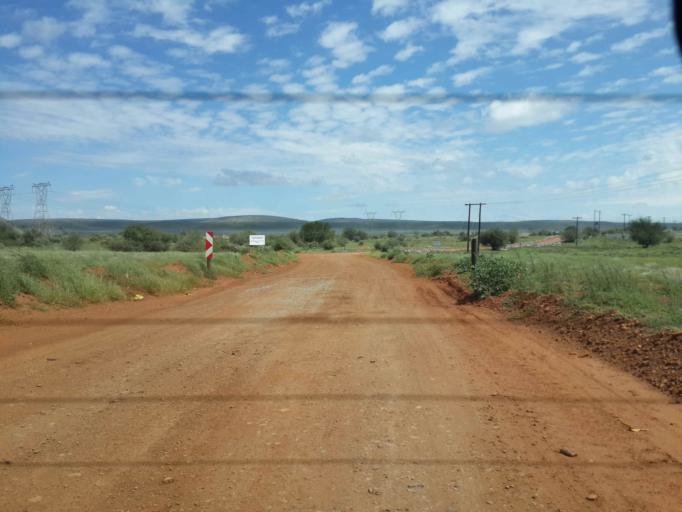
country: ZA
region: Northern Cape
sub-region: Siyanda District Municipality
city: Danielskuil
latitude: -28.2016
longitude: 23.5439
